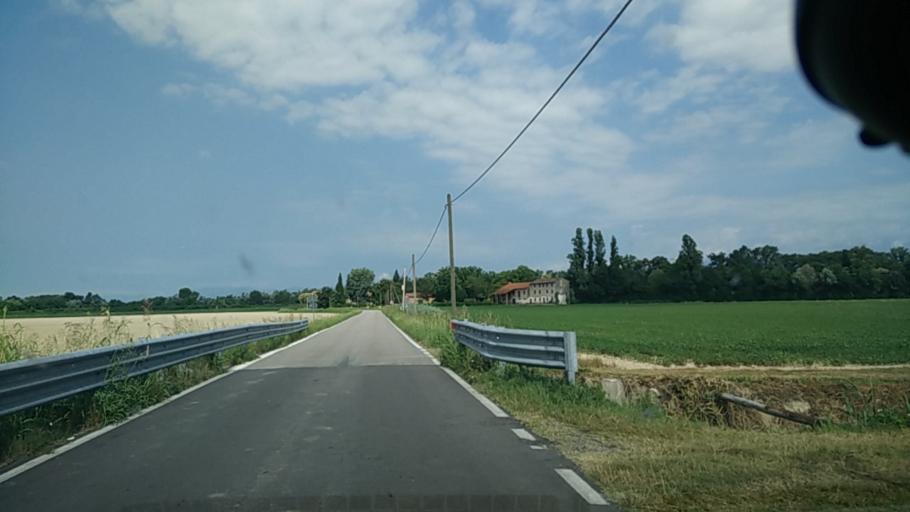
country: IT
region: Friuli Venezia Giulia
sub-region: Provincia di Pordenone
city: Puia-Villanova
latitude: 45.8313
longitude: 12.5805
